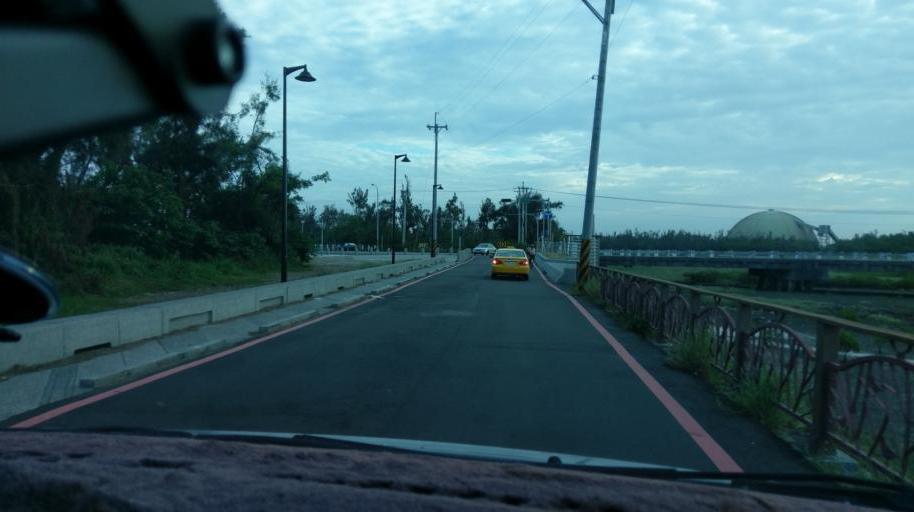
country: TW
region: Taiwan
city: Fengyuan
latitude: 24.3005
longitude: 120.5464
